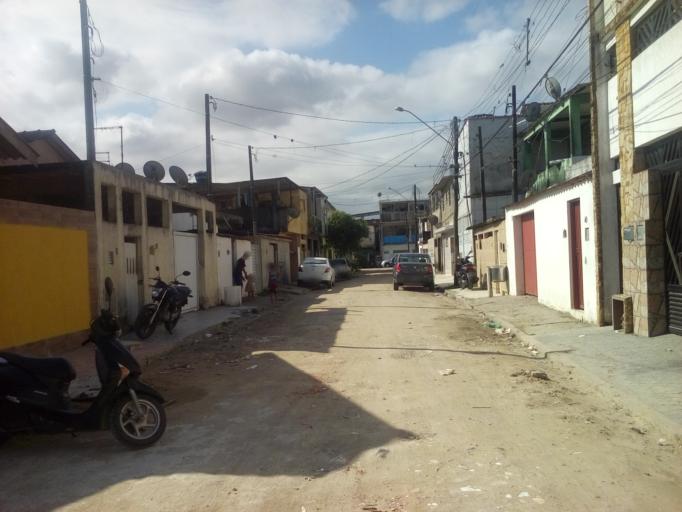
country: BR
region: Sao Paulo
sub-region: Guaruja
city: Guaruja
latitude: -23.9625
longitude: -46.2538
